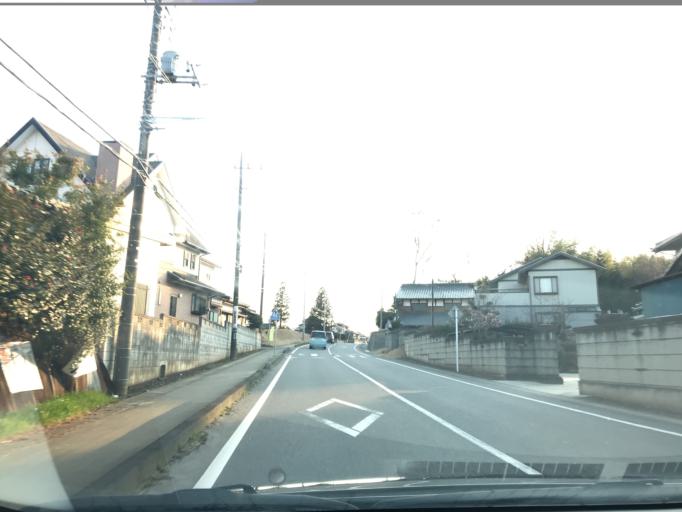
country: JP
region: Ibaraki
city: Ushiku
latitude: 36.0180
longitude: 140.0698
